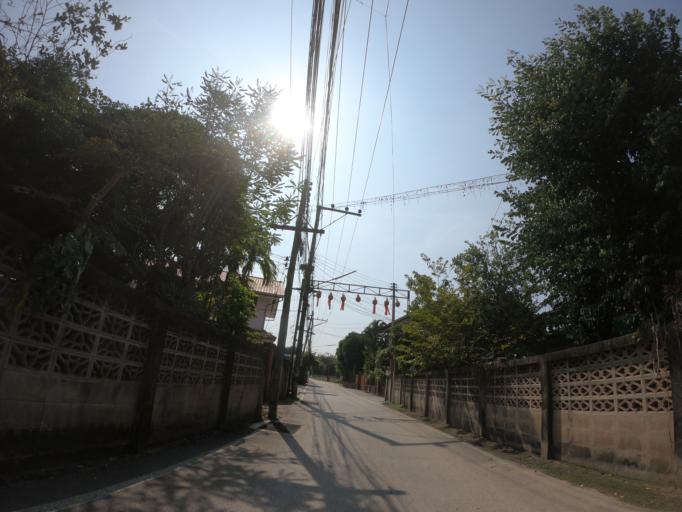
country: TH
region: Chiang Mai
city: Saraphi
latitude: 18.7581
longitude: 99.0280
